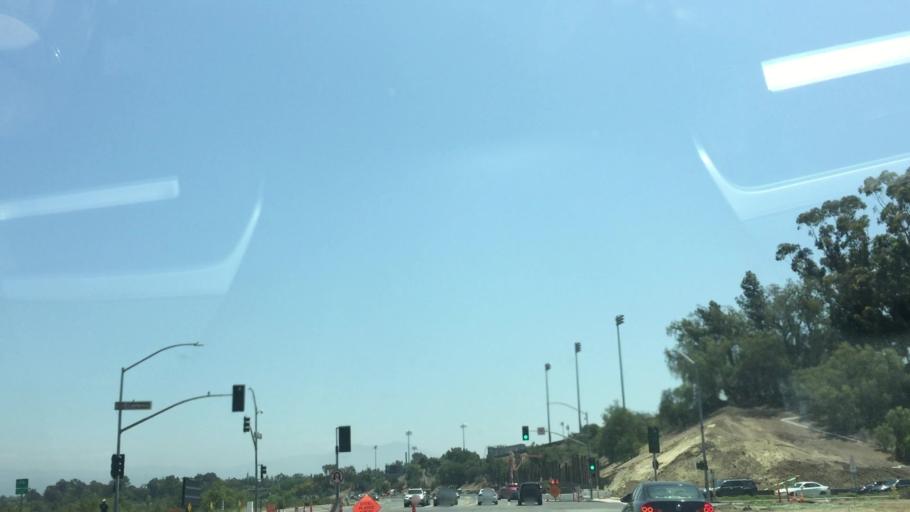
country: US
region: California
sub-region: Orange County
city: Irvine
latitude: 33.6507
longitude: -117.8541
